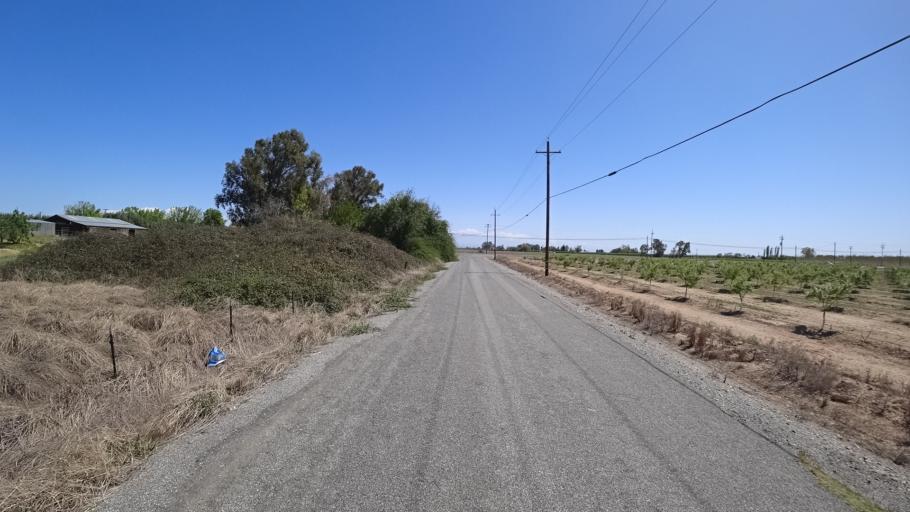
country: US
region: California
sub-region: Glenn County
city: Orland
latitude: 39.7892
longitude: -122.1989
